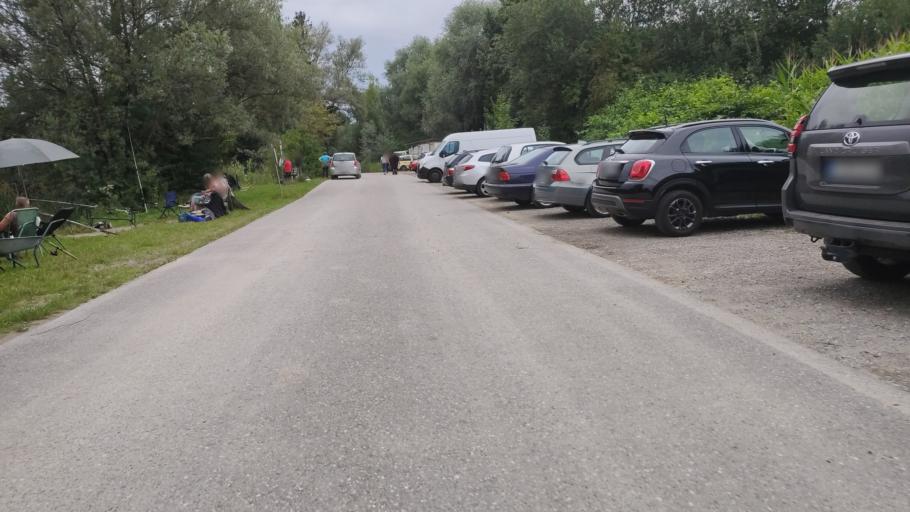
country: DE
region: Bavaria
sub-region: Swabia
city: Konigsbrunn
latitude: 48.2466
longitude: 10.8823
